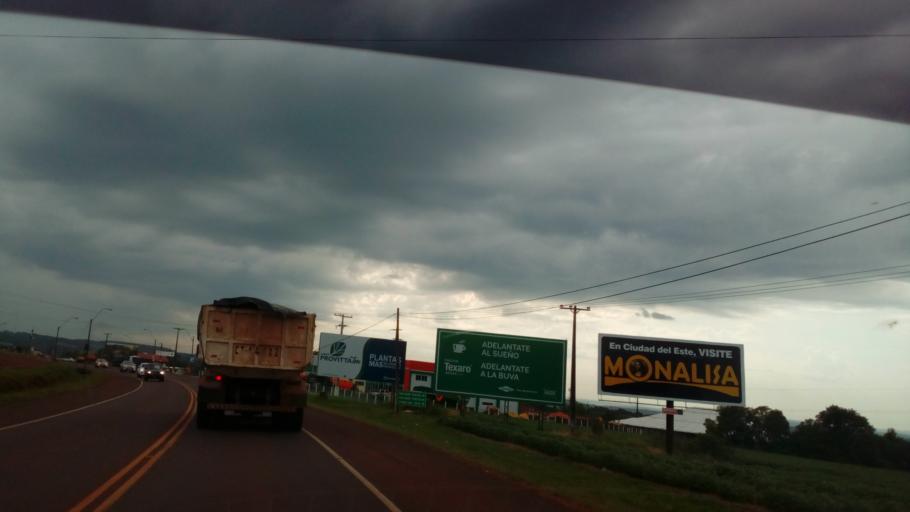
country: PY
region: Itapua
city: Obligado
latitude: -27.0734
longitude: -55.6185
